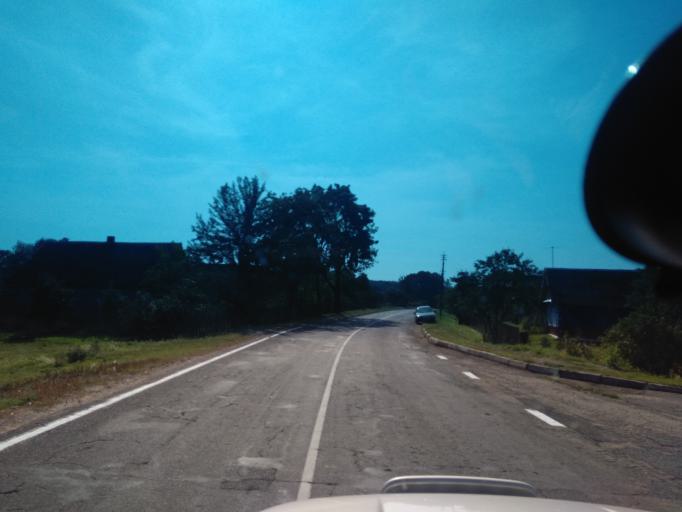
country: BY
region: Minsk
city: Uzda
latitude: 53.3895
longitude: 27.2427
